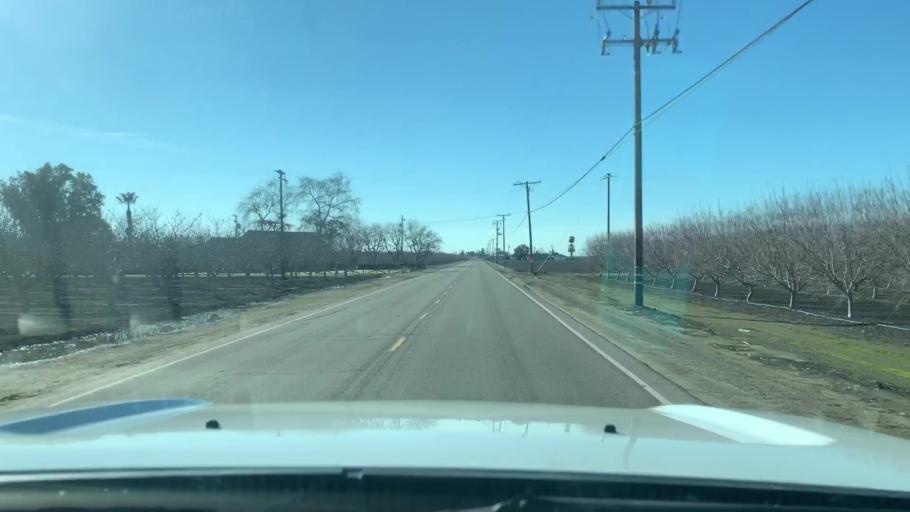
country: US
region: California
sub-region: Tulare County
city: Tulare
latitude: 36.1813
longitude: -119.4475
